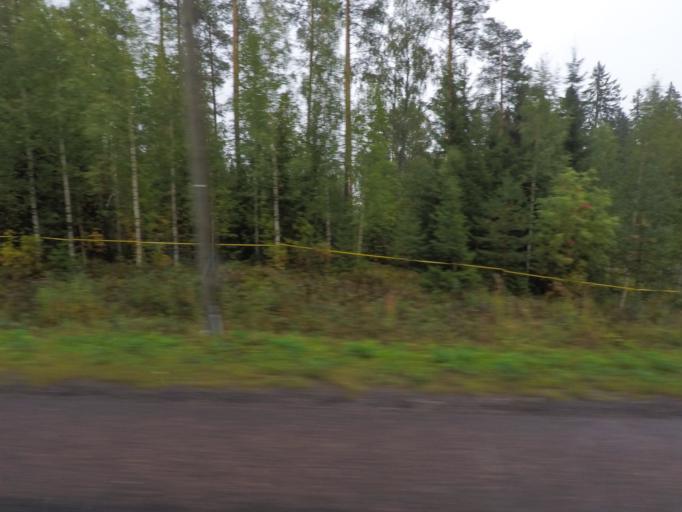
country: FI
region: Northern Savo
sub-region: Varkaus
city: Leppaevirta
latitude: 62.4249
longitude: 27.8166
